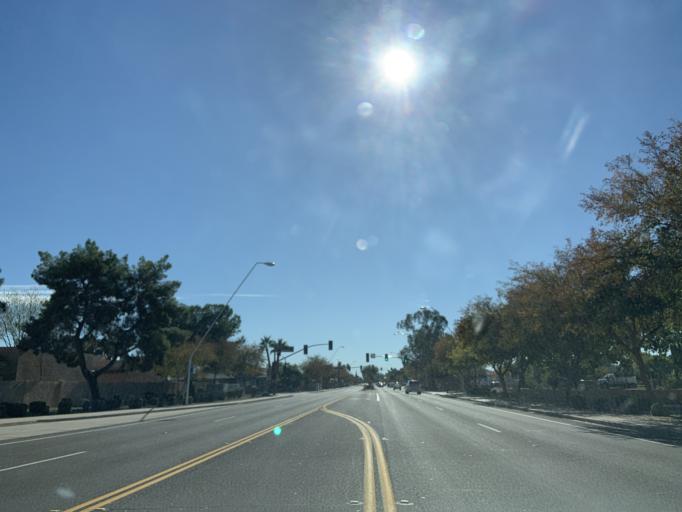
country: US
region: Arizona
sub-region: Maricopa County
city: San Carlos
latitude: 33.3549
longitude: -111.8592
